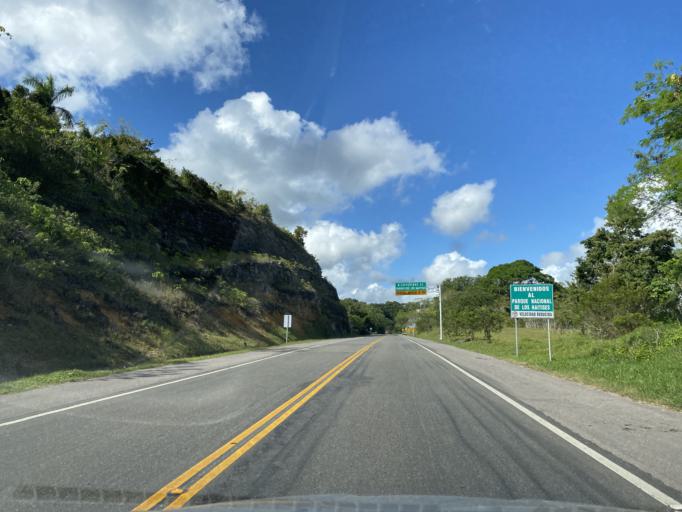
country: DO
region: Monte Plata
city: Majagual
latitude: 19.0432
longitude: -69.8303
